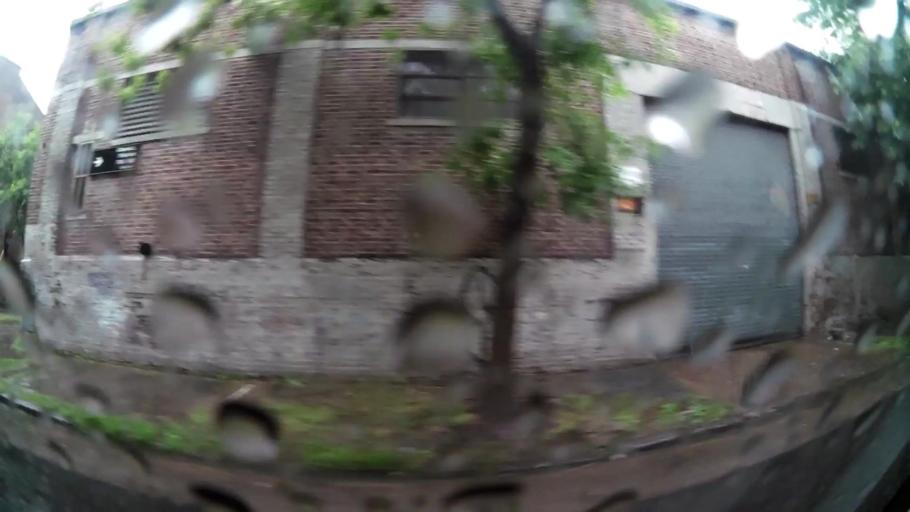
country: AR
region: Buenos Aires
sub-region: Partido de Avellaneda
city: Avellaneda
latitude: -34.6419
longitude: -58.3613
